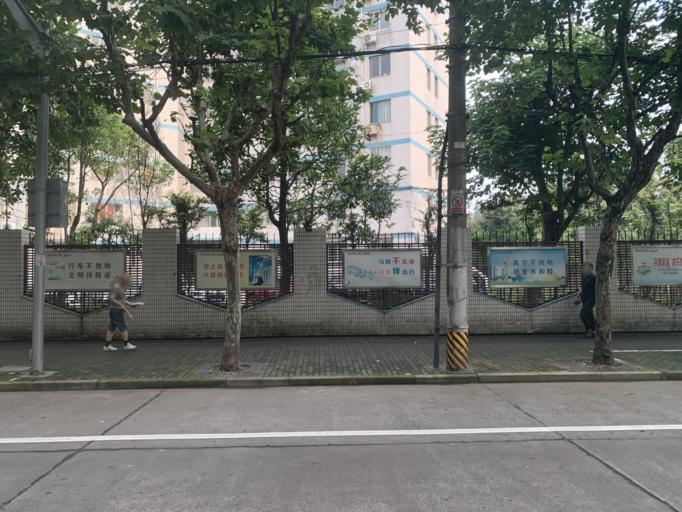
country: CN
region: Shanghai Shi
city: Huamu
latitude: 31.2441
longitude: 121.5675
